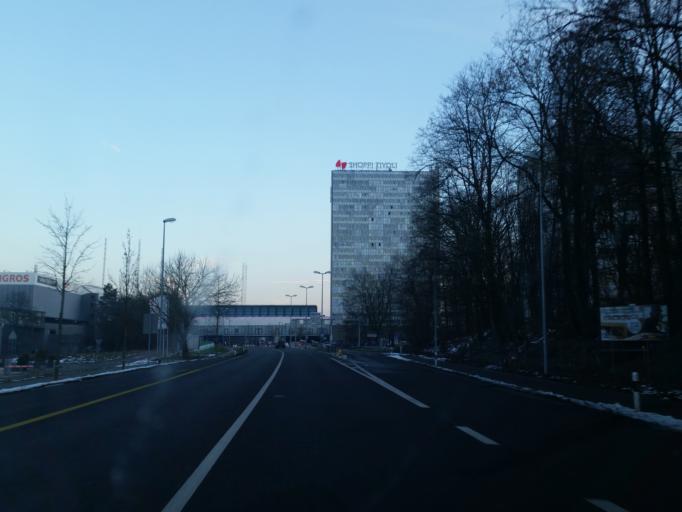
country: CH
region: Aargau
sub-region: Bezirk Baden
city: Spreitenbach
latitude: 47.4243
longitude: 8.3663
